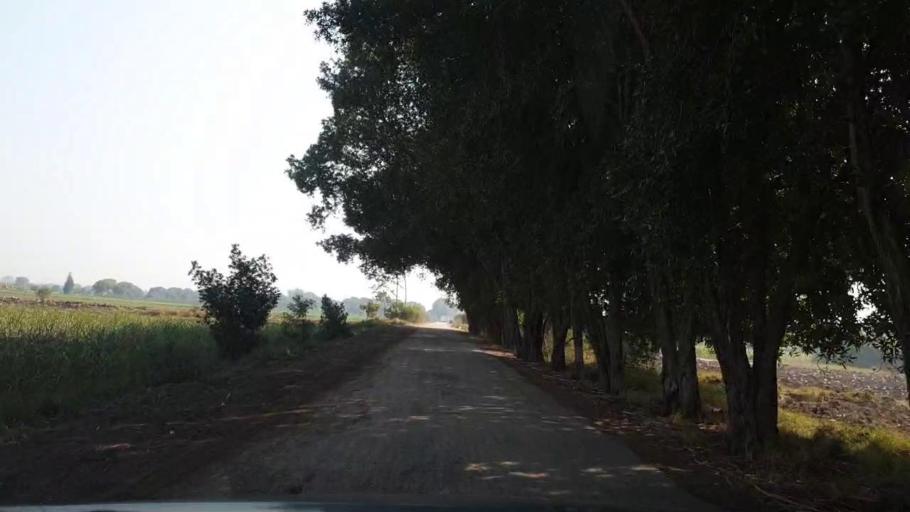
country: PK
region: Sindh
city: Matiari
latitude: 25.5589
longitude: 68.4891
